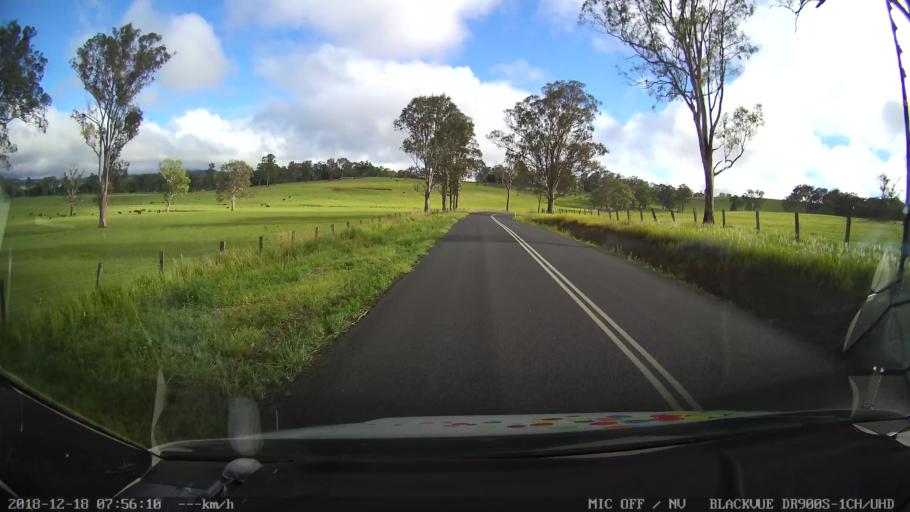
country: AU
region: New South Wales
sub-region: Kyogle
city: Kyogle
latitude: -28.4013
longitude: 152.6043
